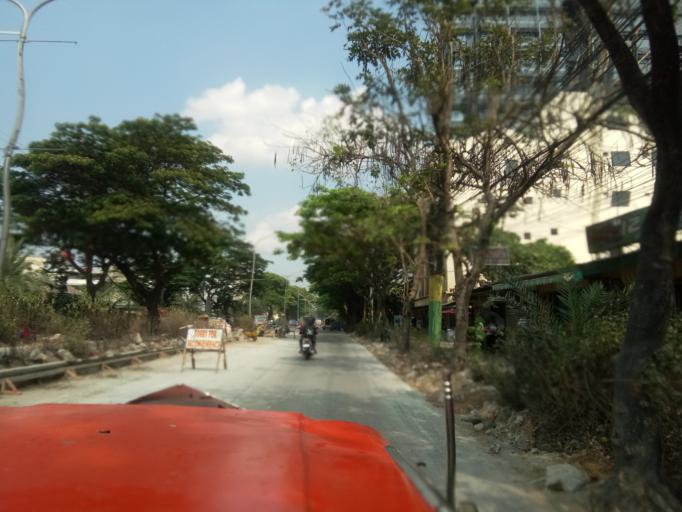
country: PH
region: Calabarzon
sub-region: Province of Cavite
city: Dasmarinas
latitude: 14.3267
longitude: 120.9446
